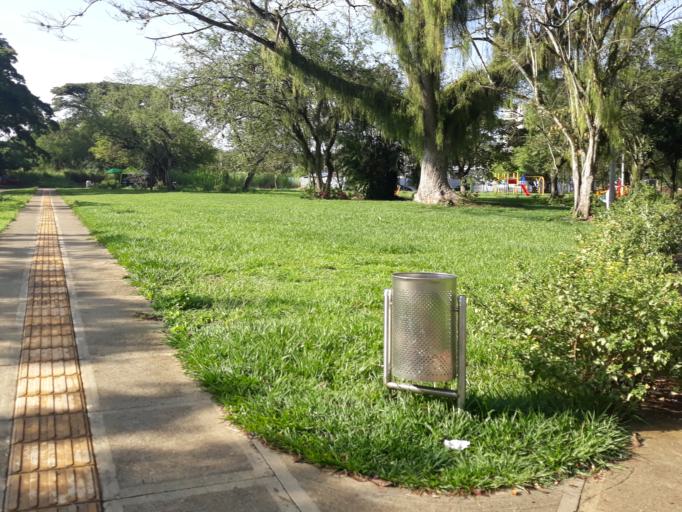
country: CO
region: Valle del Cauca
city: Cali
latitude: 3.3561
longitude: -76.5195
